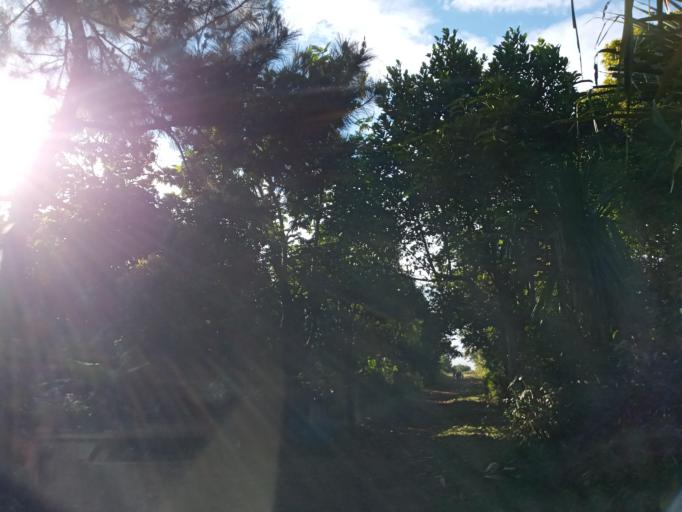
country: MG
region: Atsimo-Atsinanana
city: Vohipaho
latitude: -23.5563
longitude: 47.6251
